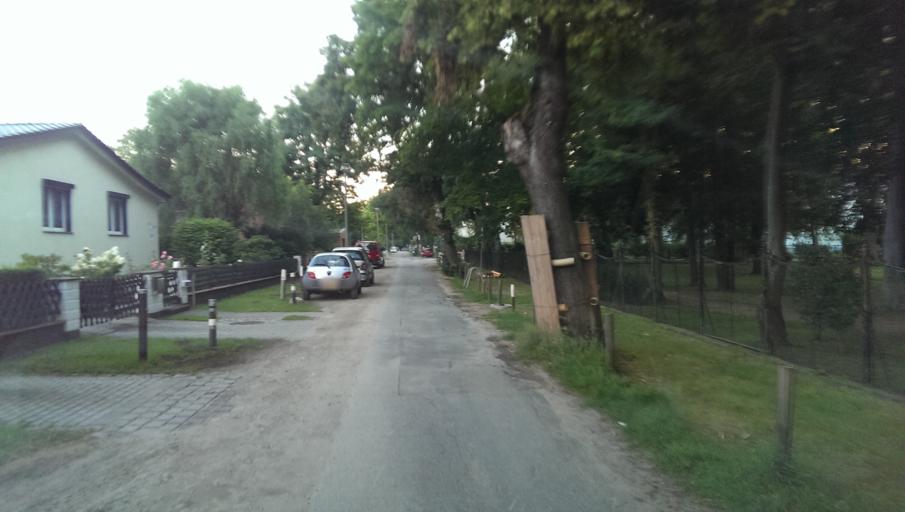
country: DE
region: Brandenburg
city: Teltow
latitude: 52.4091
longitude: 13.2881
